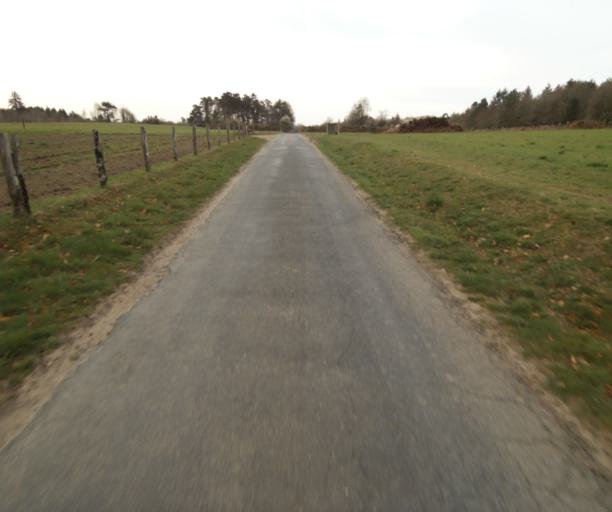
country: FR
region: Limousin
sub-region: Departement de la Correze
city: Correze
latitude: 45.4453
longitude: 1.8207
